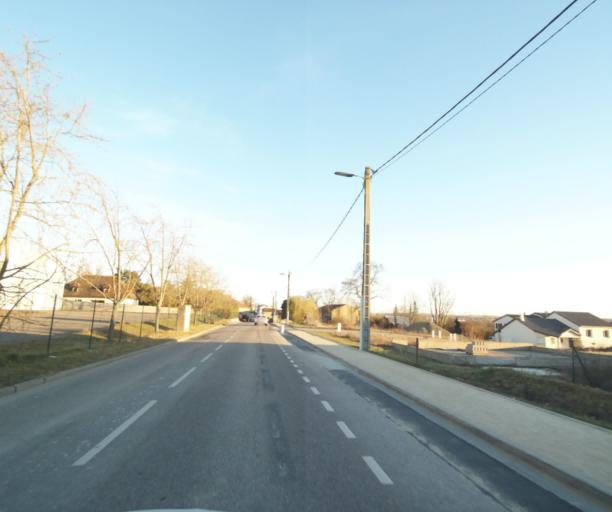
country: FR
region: Lorraine
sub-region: Departement de Meurthe-et-Moselle
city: Tomblaine
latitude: 48.6737
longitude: 6.2246
